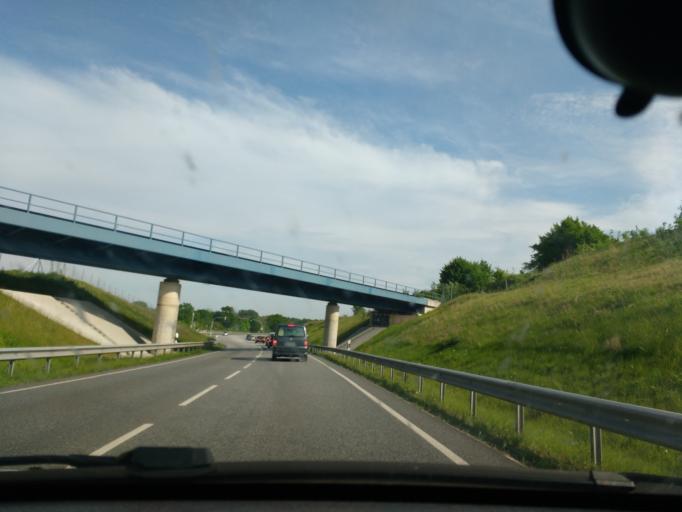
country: DE
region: Schleswig-Holstein
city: Pogeez
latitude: 53.7438
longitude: 10.7269
